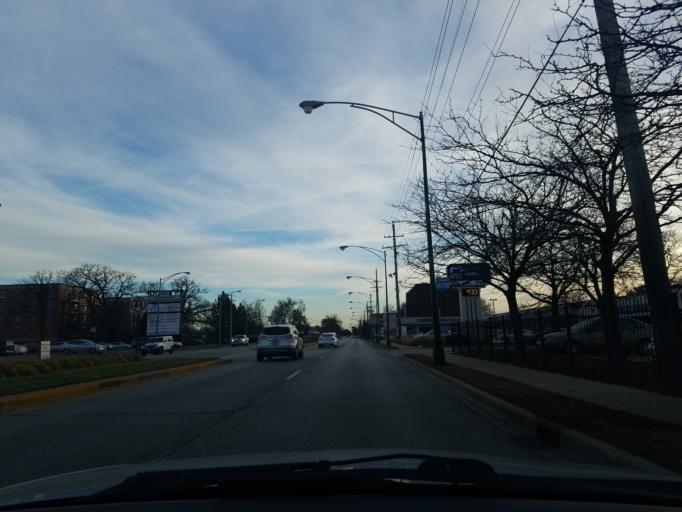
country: US
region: Illinois
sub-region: Cook County
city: Norridge
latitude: 41.9655
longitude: -87.8368
